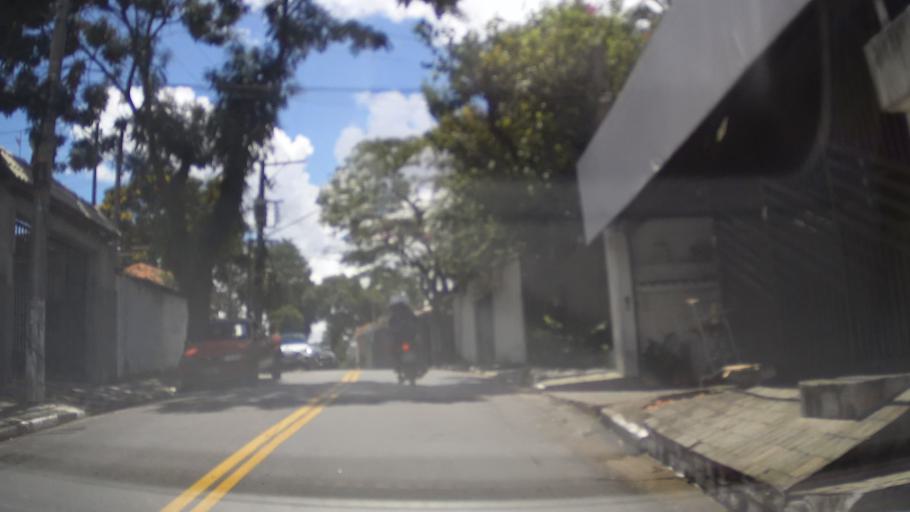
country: BR
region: Sao Paulo
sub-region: Guarulhos
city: Guarulhos
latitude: -23.4547
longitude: -46.5381
